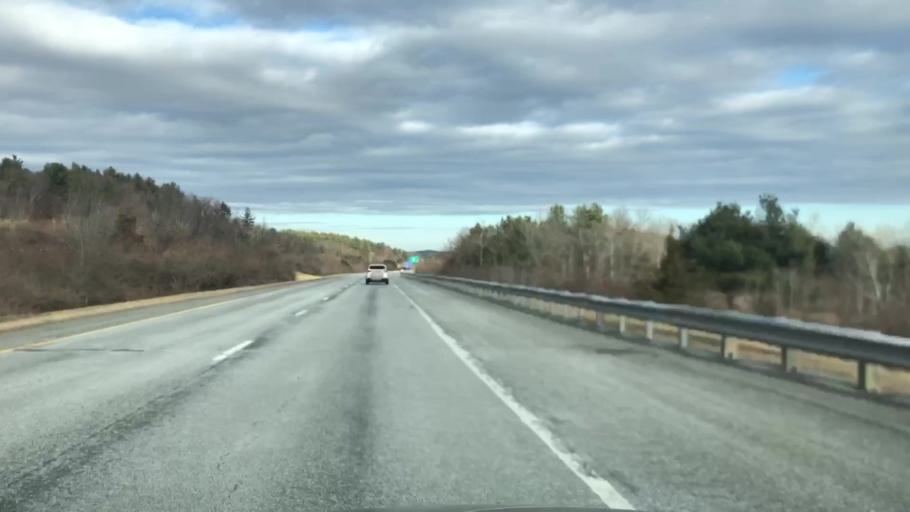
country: US
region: Massachusetts
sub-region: Worcester County
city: Sterling
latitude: 42.4511
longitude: -71.7566
